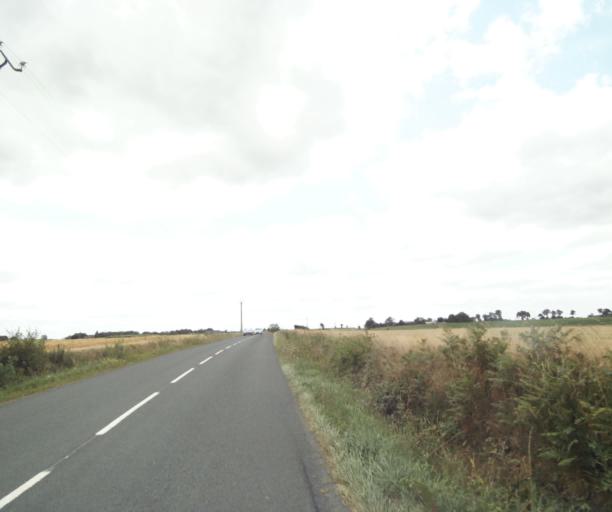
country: FR
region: Pays de la Loire
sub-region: Departement de la Sarthe
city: Sable-sur-Sarthe
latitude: 47.8584
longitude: -0.3319
